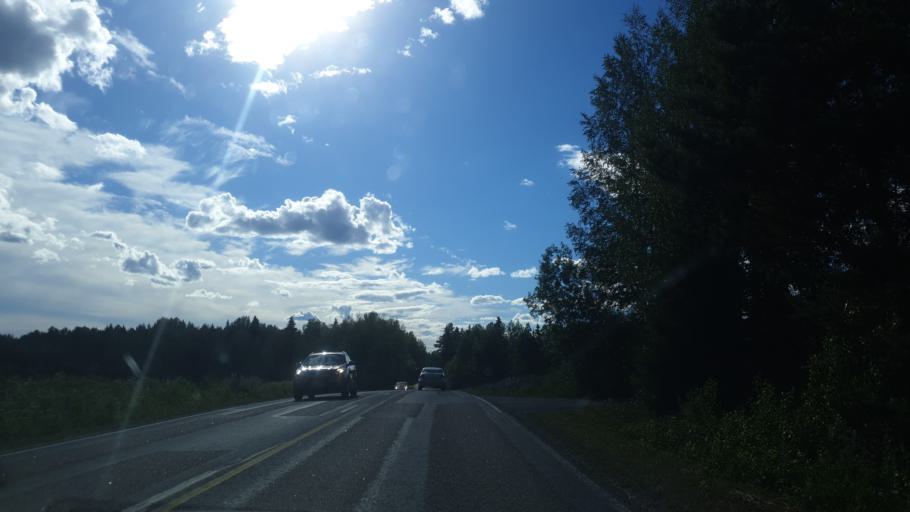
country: FI
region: Southern Savonia
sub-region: Mikkeli
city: Pertunmaa
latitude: 61.5227
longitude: 26.5589
